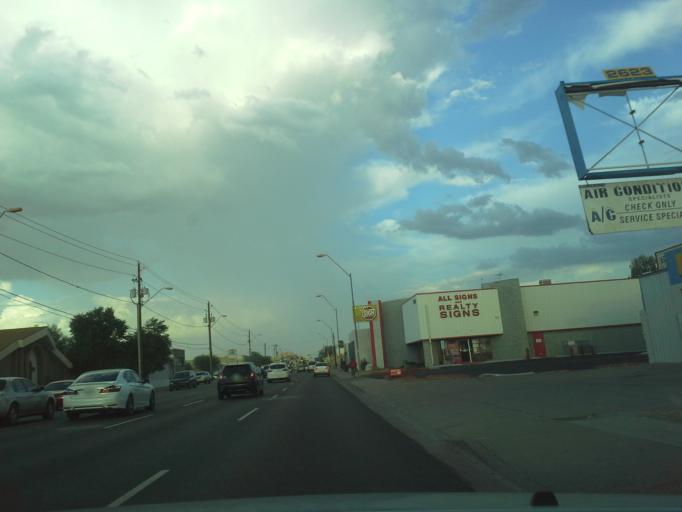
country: US
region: Arizona
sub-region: Maricopa County
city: Phoenix
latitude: 33.4657
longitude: -112.0252
